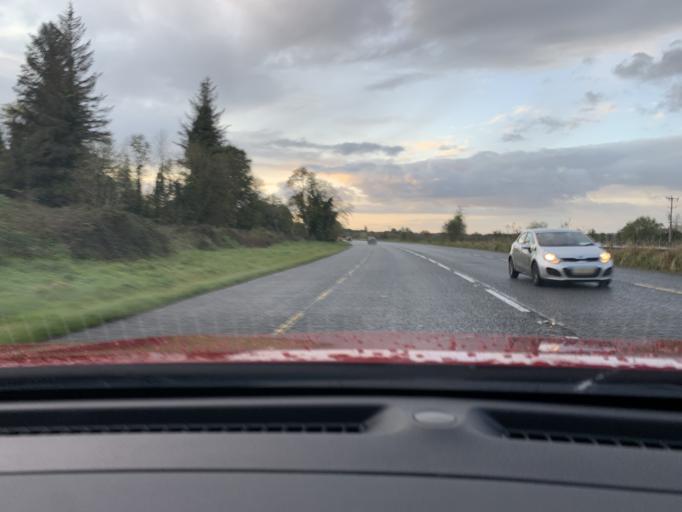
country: IE
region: Connaught
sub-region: County Leitrim
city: Carrick-on-Shannon
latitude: 53.9474
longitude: -8.1226
